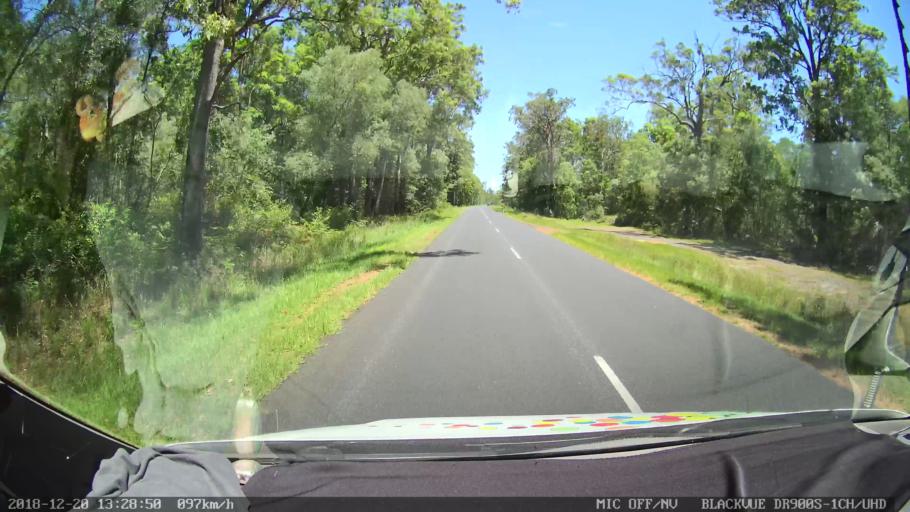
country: AU
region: New South Wales
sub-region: Clarence Valley
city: Gordon
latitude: -29.1803
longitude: 152.9894
